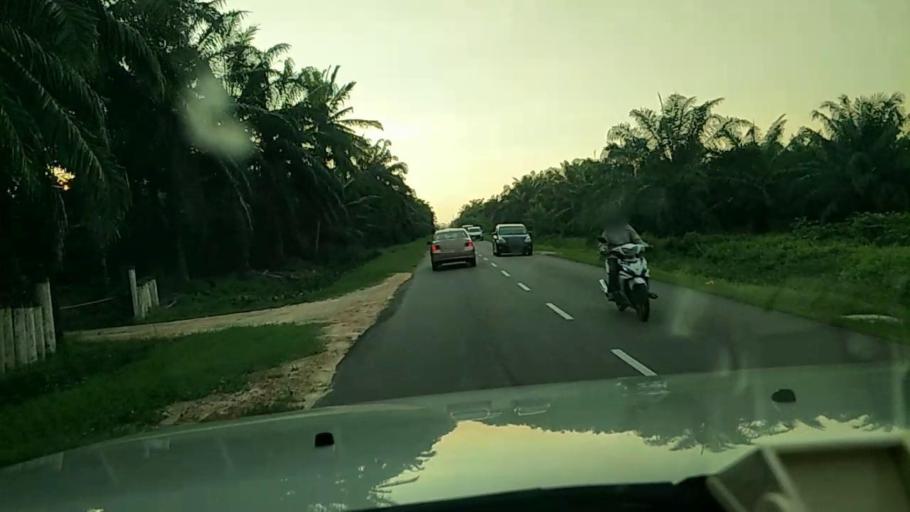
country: MY
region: Selangor
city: Kuala Selangor
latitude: 3.3182
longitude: 101.2789
